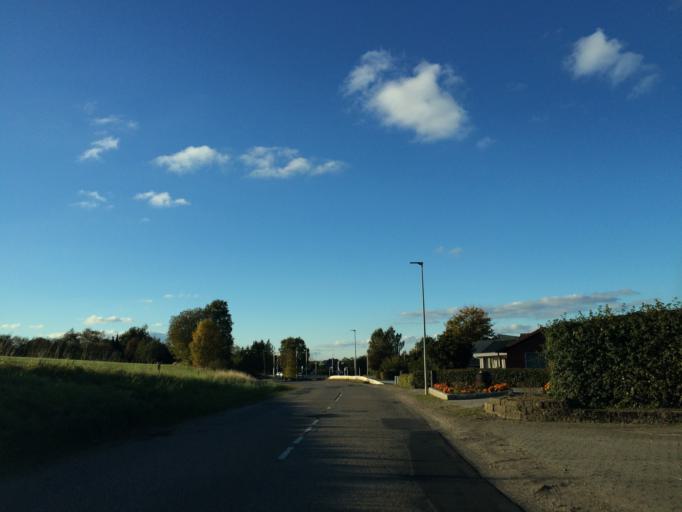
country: DK
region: Central Jutland
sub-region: Silkeborg Kommune
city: Svejbaek
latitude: 56.1508
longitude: 9.6979
